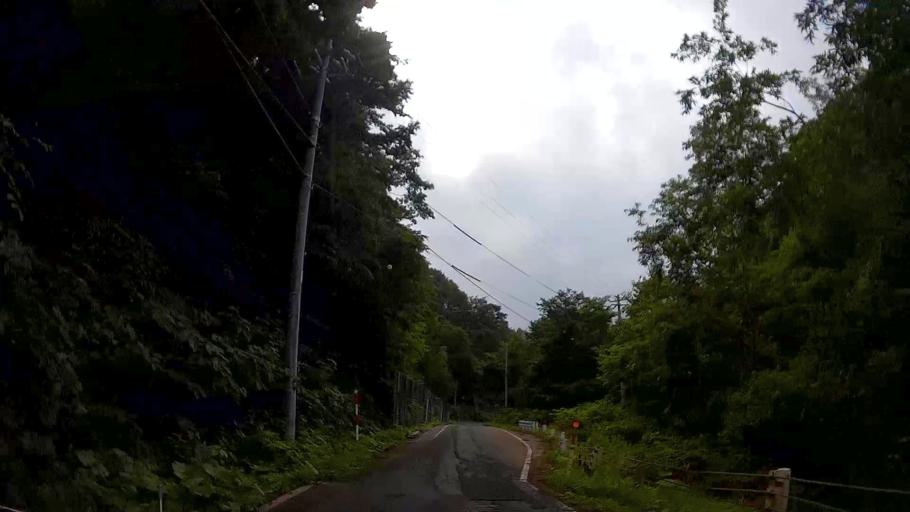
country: JP
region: Hokkaido
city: Nanae
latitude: 42.0748
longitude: 140.5318
